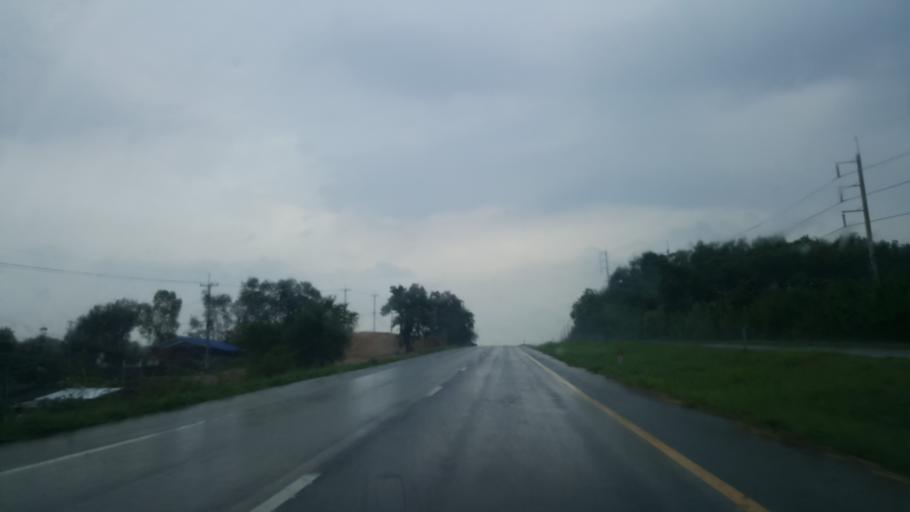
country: TH
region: Chon Buri
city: Ban Talat Bueng
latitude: 12.9880
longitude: 101.0610
